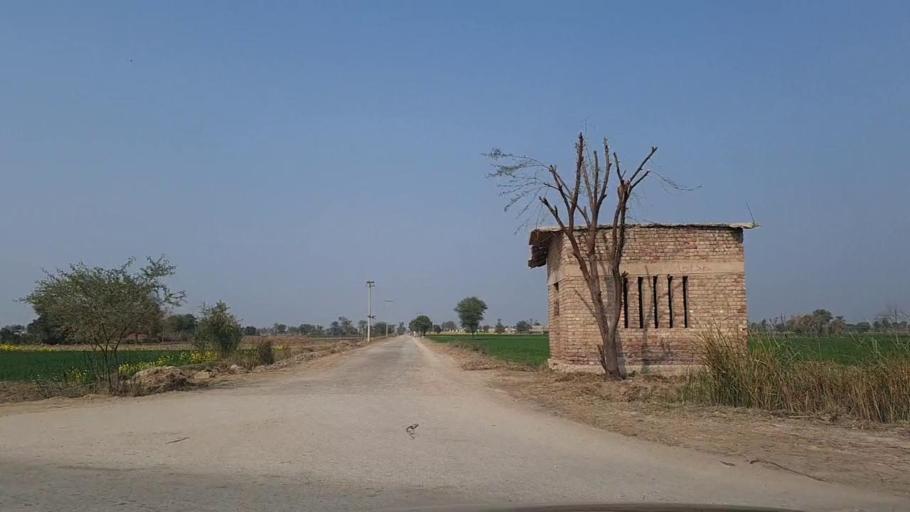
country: PK
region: Sindh
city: Daur
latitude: 26.4045
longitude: 68.4240
